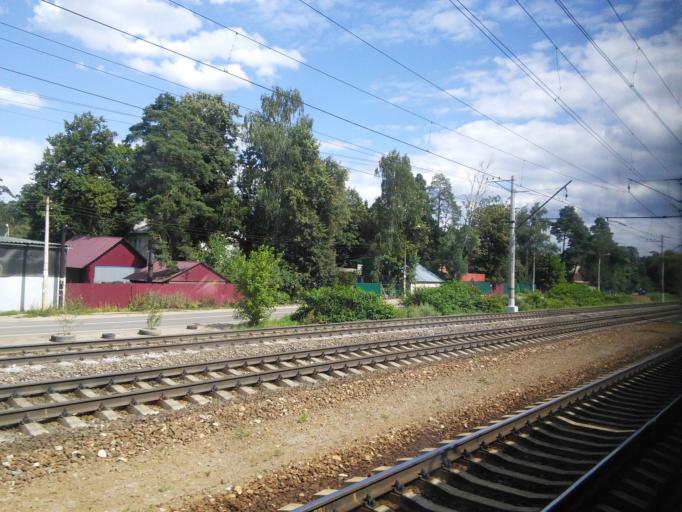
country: RU
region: Moskovskaya
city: Malakhovka
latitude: 55.6424
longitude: 38.0190
